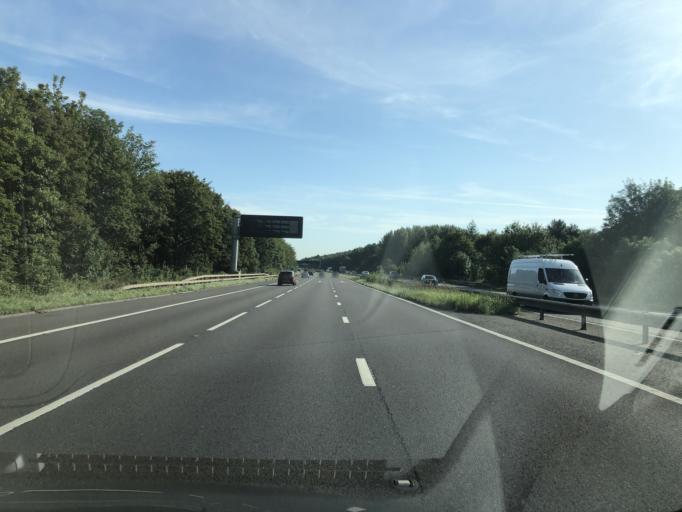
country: GB
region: England
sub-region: Doncaster
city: Stainton
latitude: 53.4696
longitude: -1.1716
